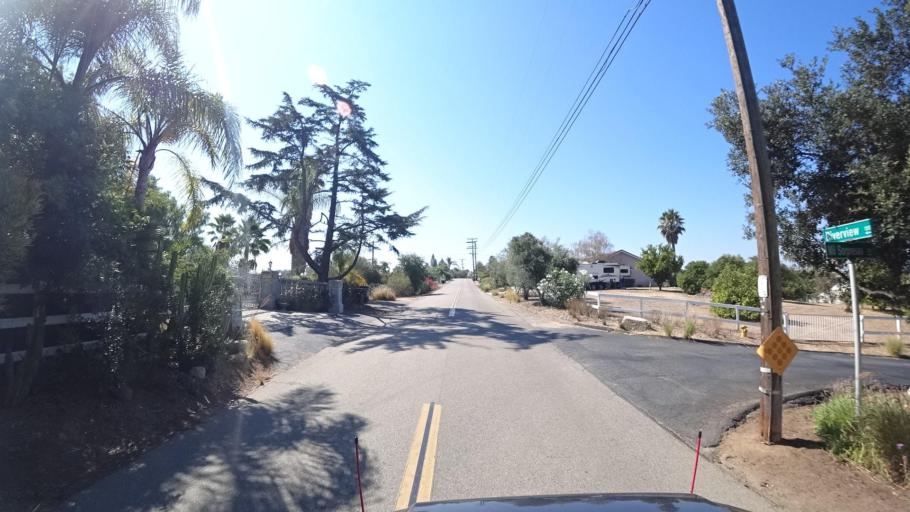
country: US
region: California
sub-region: San Diego County
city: Fallbrook
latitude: 33.3968
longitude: -117.2150
